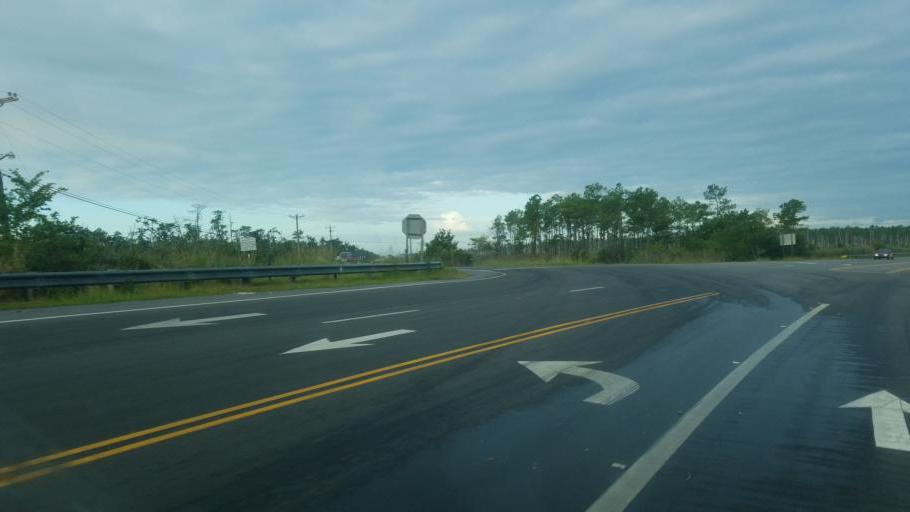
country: US
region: North Carolina
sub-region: Dare County
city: Manteo
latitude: 35.8715
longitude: -75.7846
